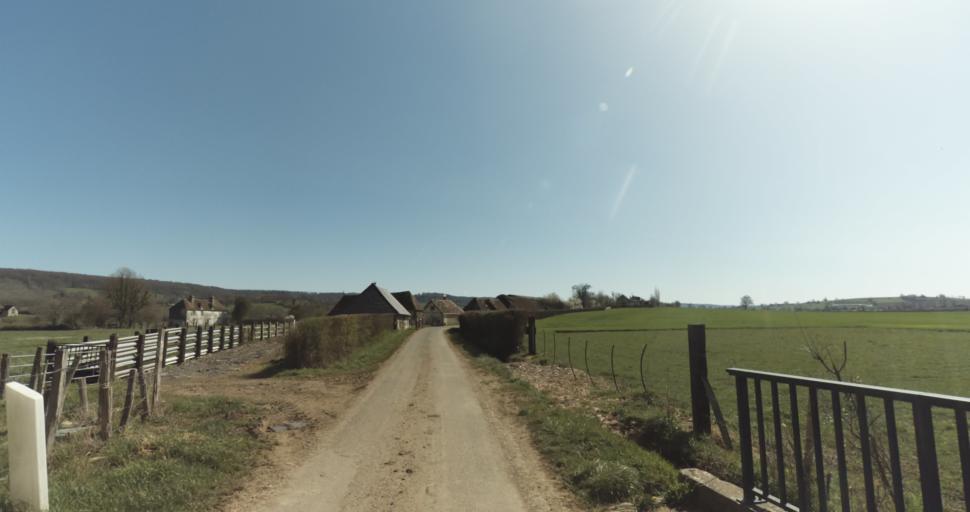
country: FR
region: Lower Normandy
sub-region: Departement du Calvados
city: Saint-Pierre-sur-Dives
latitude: 49.0077
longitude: 0.0174
